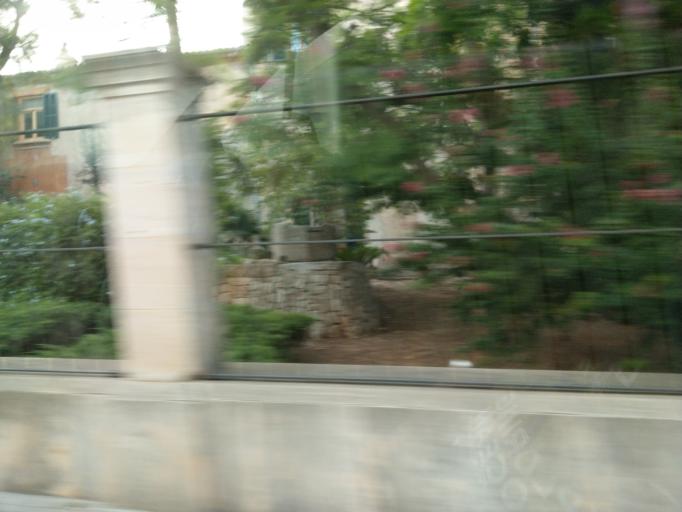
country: ES
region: Balearic Islands
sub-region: Illes Balears
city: Ses Salines
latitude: 39.3392
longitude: 3.0558
